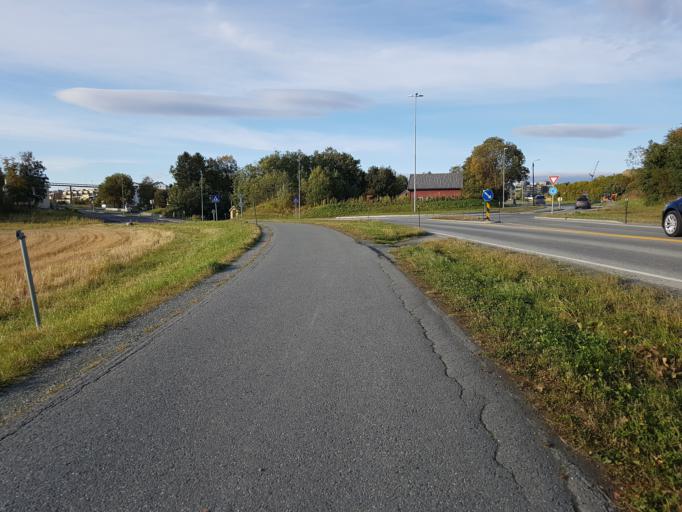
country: NO
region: Sor-Trondelag
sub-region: Trondheim
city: Trondheim
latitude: 63.3822
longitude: 10.4349
